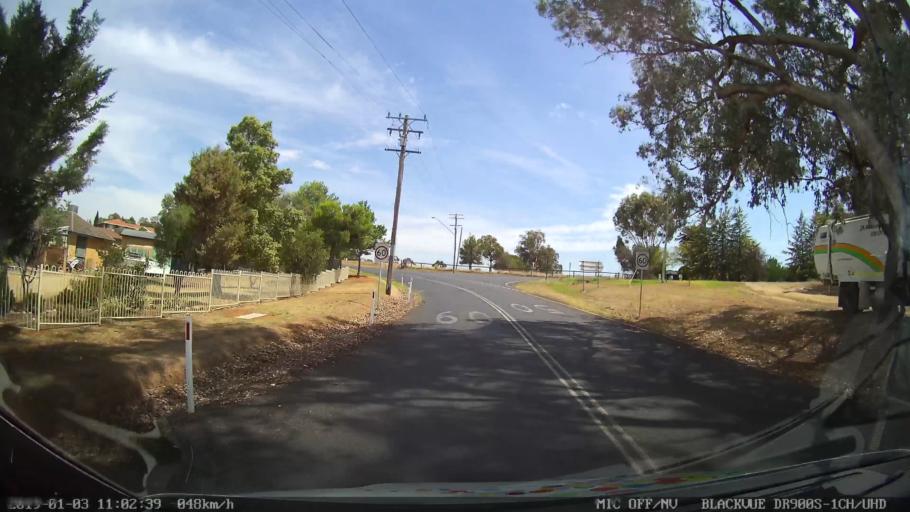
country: AU
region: New South Wales
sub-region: Young
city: Young
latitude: -34.2964
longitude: 148.2983
